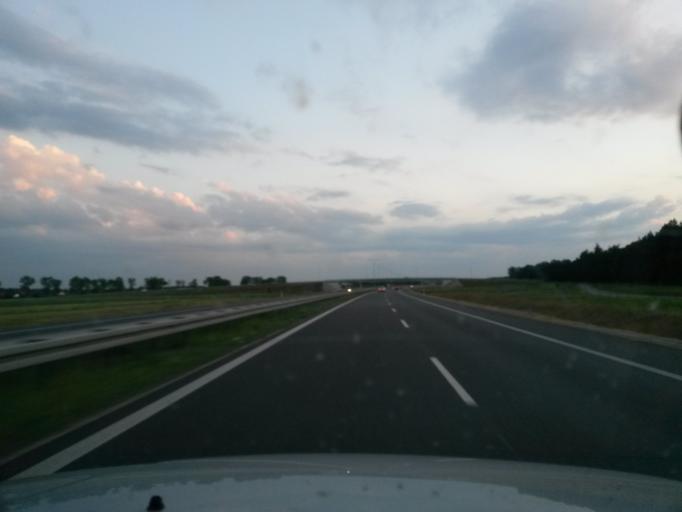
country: PL
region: Lower Silesian Voivodeship
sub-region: Powiat olesnicki
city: Olesnica
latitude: 51.2336
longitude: 17.4835
